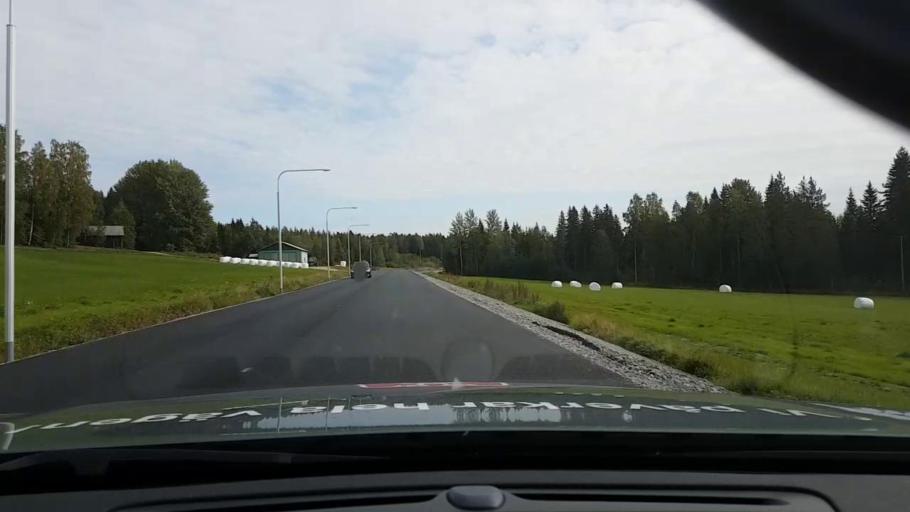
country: SE
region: Vaesternorrland
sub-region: OErnskoeldsviks Kommun
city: Bjasta
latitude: 63.2928
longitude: 18.4918
